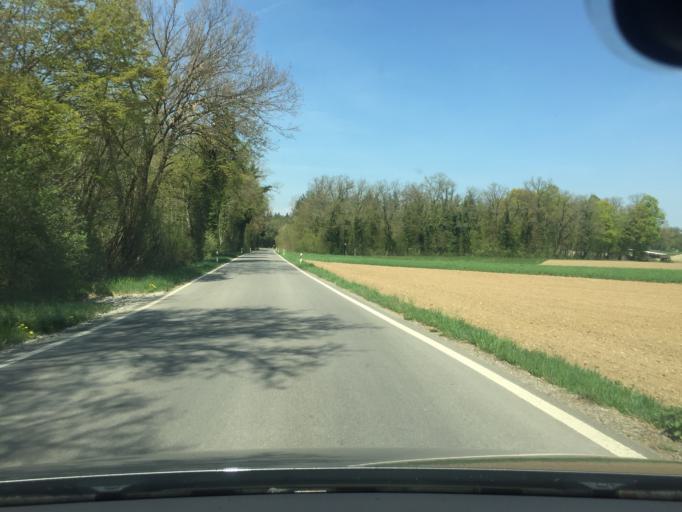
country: CH
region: Zurich
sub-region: Bezirk Andelfingen
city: Marthalen
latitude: 47.6185
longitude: 8.6282
